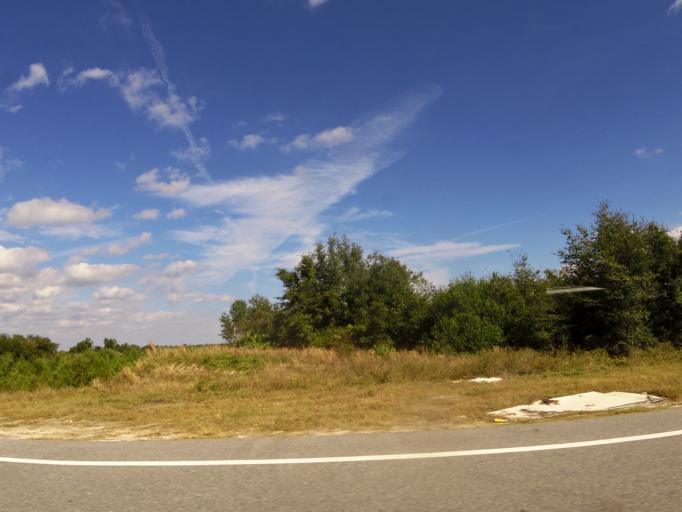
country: US
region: Florida
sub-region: Duval County
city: Jacksonville
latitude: 30.4121
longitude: -81.6248
